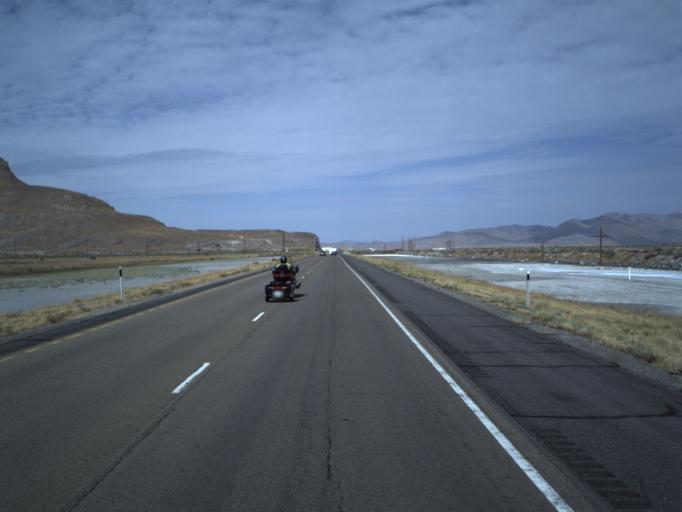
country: US
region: Utah
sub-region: Tooele County
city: Grantsville
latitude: 40.7385
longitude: -112.6162
